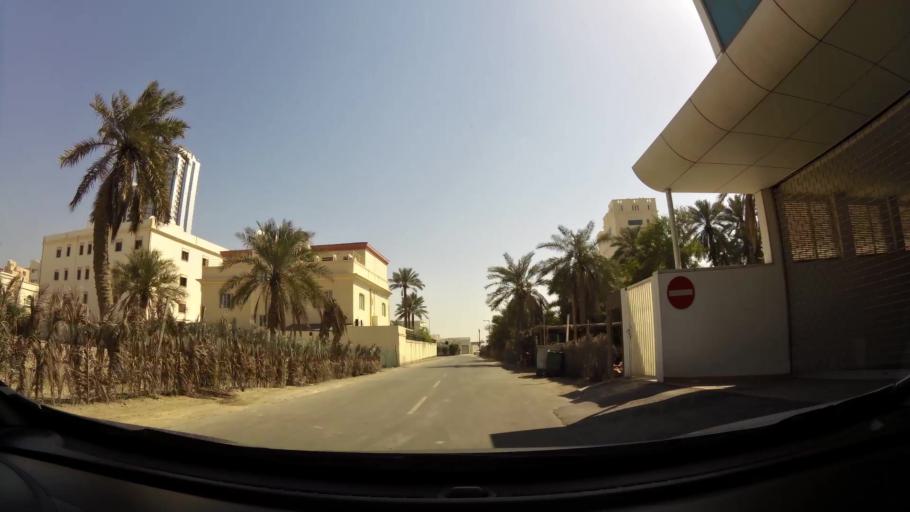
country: BH
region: Manama
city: Manama
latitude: 26.2062
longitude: 50.5773
